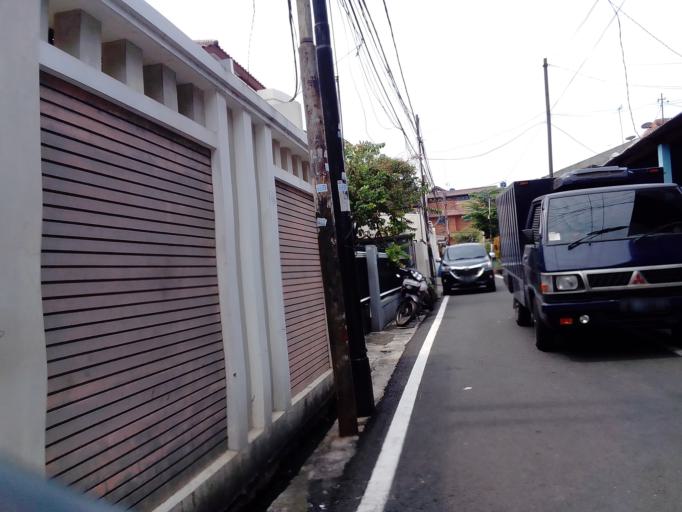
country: ID
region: Jakarta Raya
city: Jakarta
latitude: -6.1731
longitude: 106.8099
